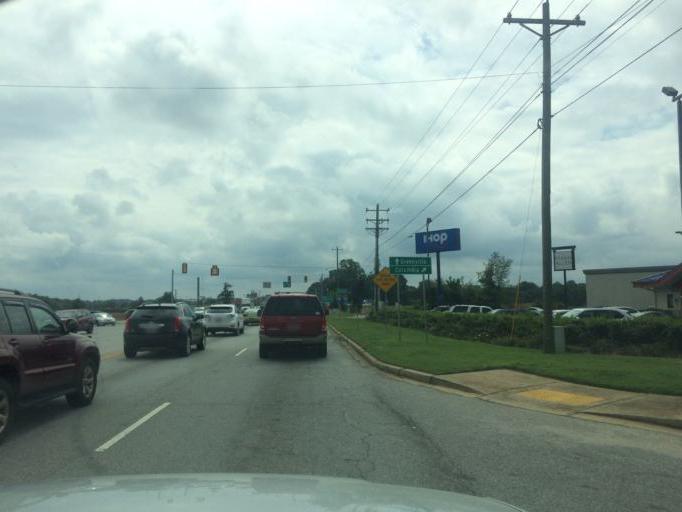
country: US
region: South Carolina
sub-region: Greenville County
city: Mauldin
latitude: 34.8244
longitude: -82.2935
